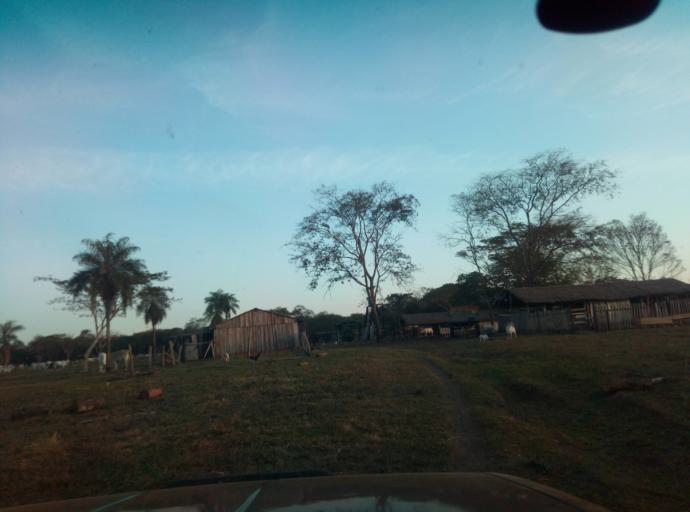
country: PY
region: Caaguazu
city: Yhu
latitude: -25.2058
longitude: -56.1054
